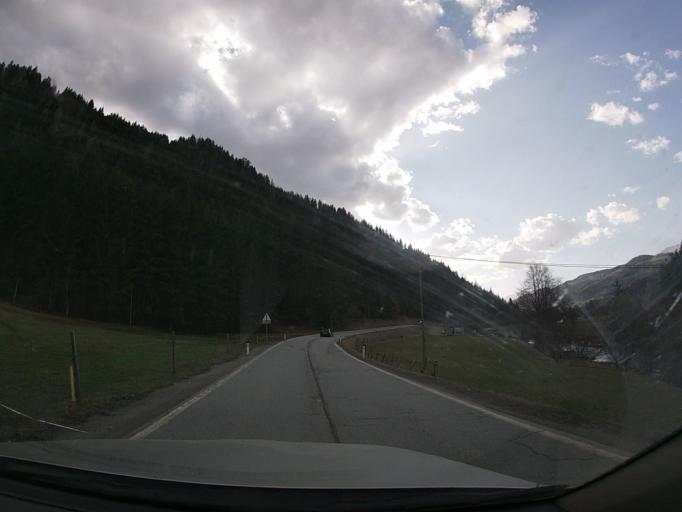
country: AT
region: Styria
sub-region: Politischer Bezirk Murau
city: Ranten
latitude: 47.1459
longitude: 14.1214
